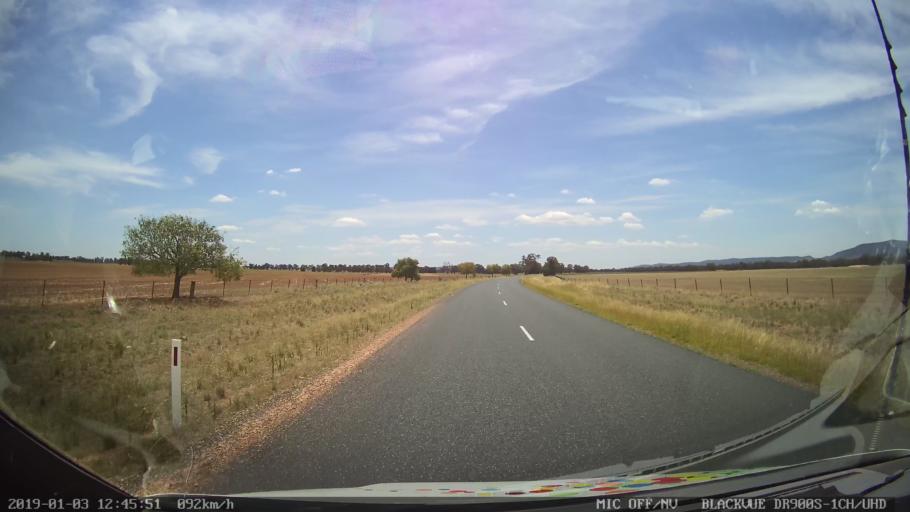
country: AU
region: New South Wales
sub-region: Weddin
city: Grenfell
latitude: -33.7444
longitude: 148.2267
